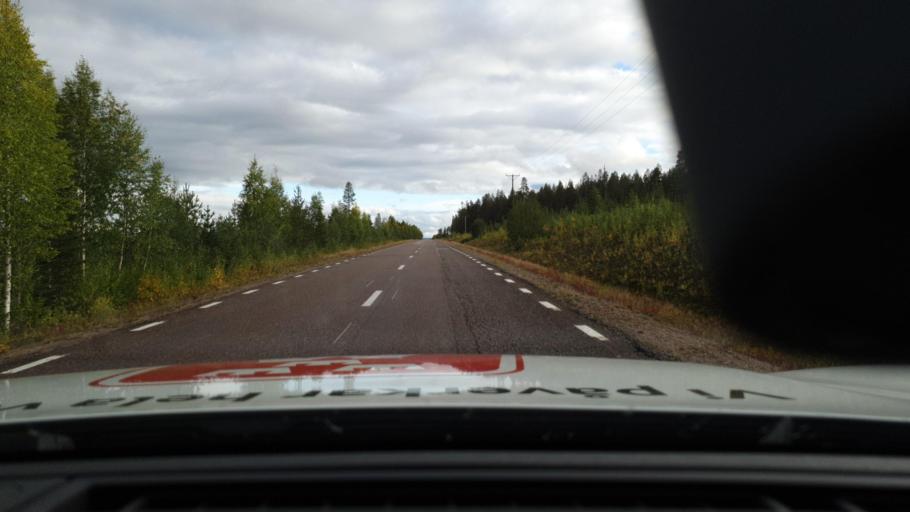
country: SE
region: Norrbotten
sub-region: Overkalix Kommun
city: OEverkalix
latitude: 67.0319
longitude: 22.5071
